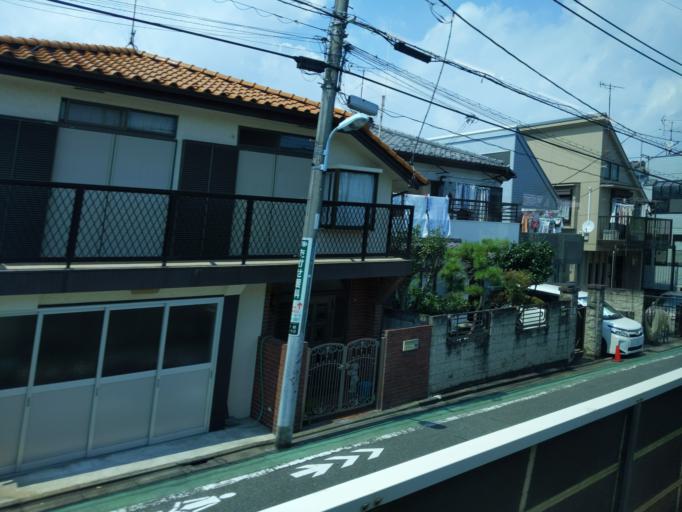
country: JP
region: Tokyo
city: Tokyo
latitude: 35.6146
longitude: 139.6734
